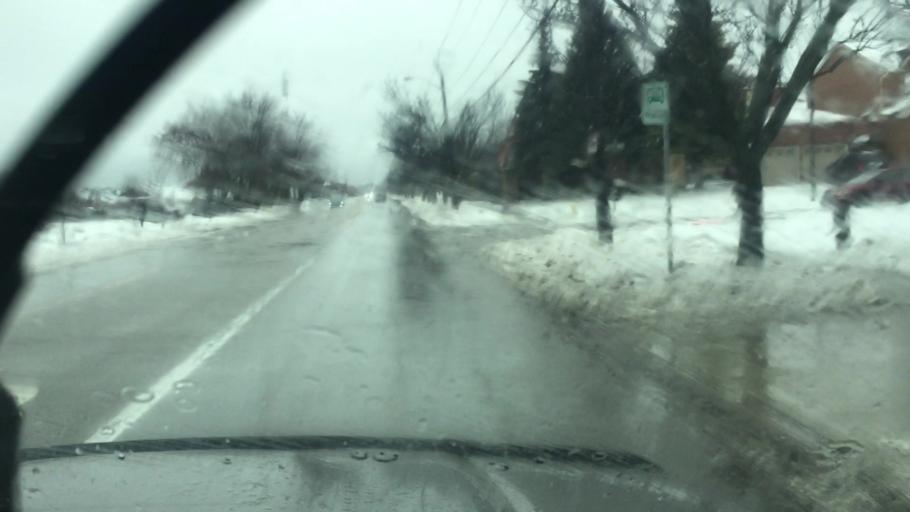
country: CA
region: Ontario
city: Ajax
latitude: 43.8596
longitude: -79.0578
